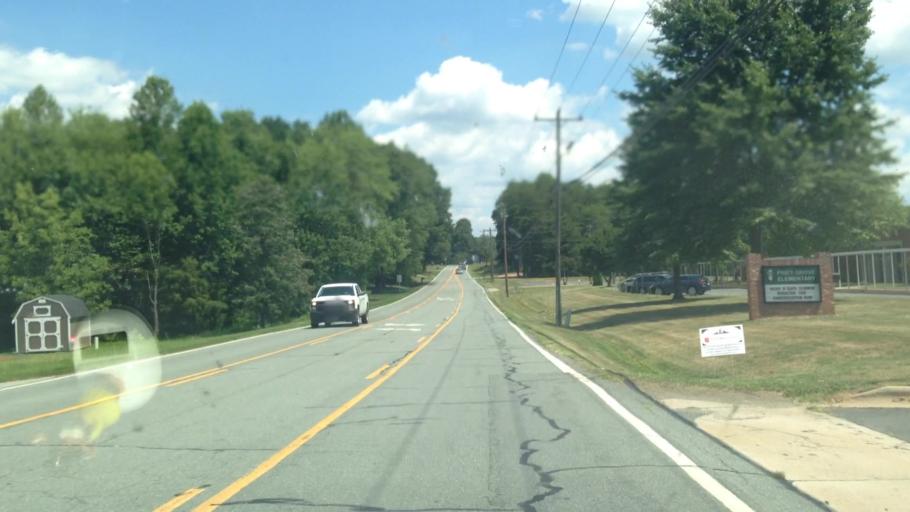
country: US
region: North Carolina
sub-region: Forsyth County
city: Kernersville
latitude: 36.1595
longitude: -80.0554
